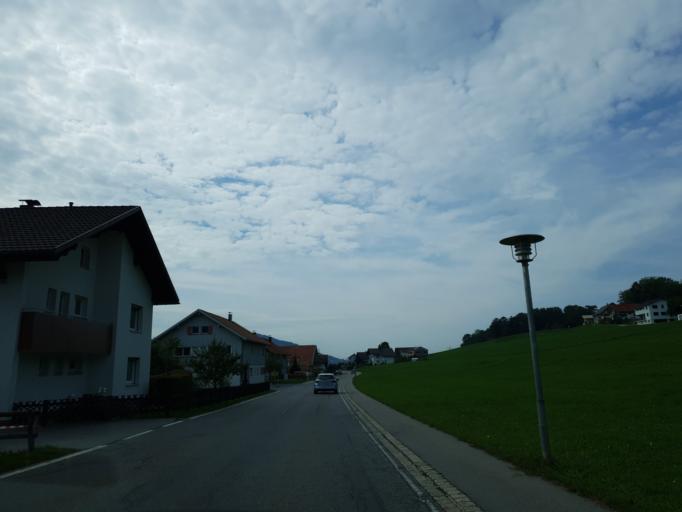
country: AT
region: Vorarlberg
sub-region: Politischer Bezirk Bregenz
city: Doren
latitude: 47.4889
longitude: 9.8652
